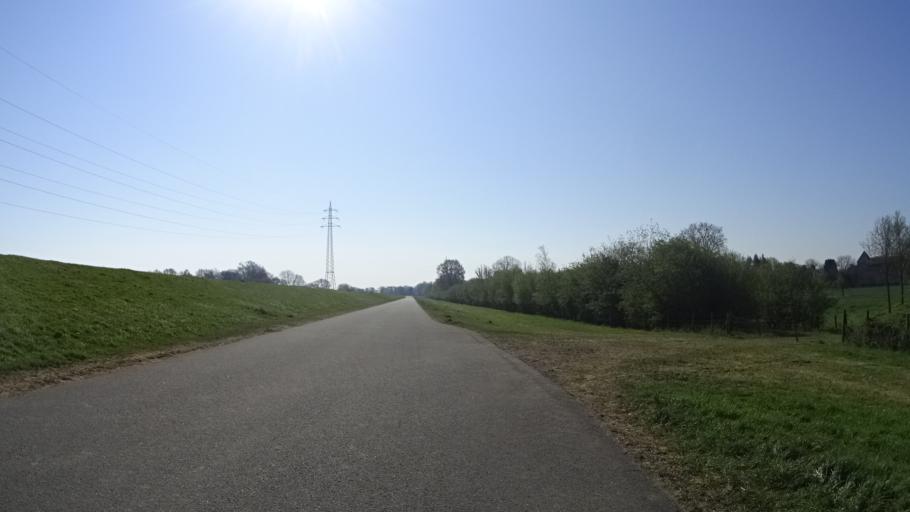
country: DE
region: North Rhine-Westphalia
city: Rheinberg
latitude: 51.5751
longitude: 6.5844
